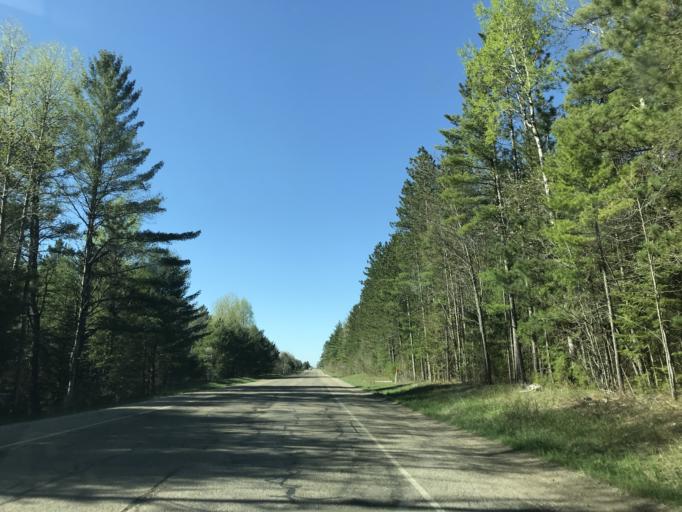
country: US
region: Michigan
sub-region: Crawford County
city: Grayling
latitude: 44.7655
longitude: -84.7545
